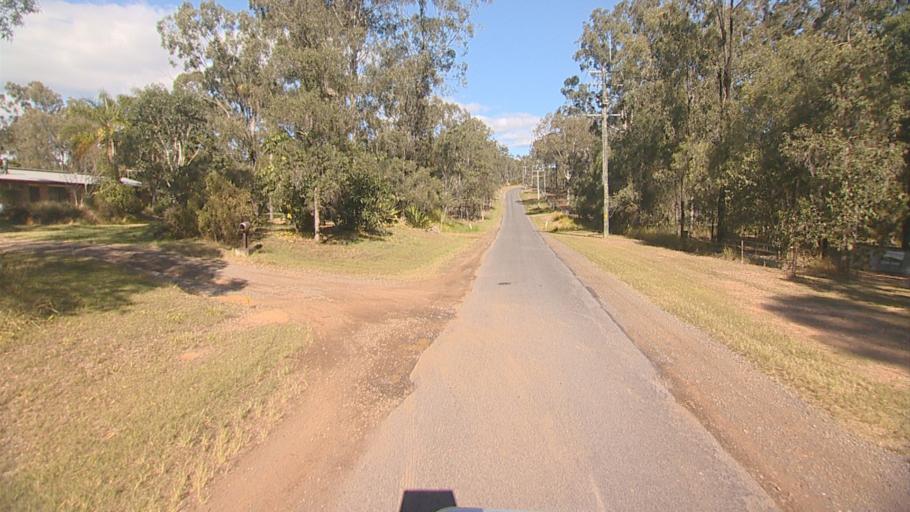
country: AU
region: Queensland
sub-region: Logan
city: Chambers Flat
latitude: -27.8050
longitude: 153.0788
